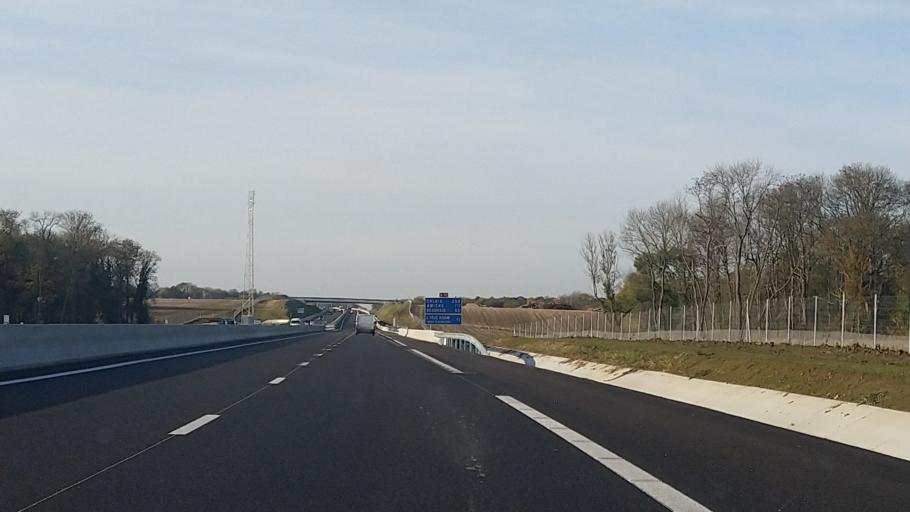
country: FR
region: Ile-de-France
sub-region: Departement du Val-d'Oise
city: Montsoult
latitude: 49.0816
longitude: 2.3275
